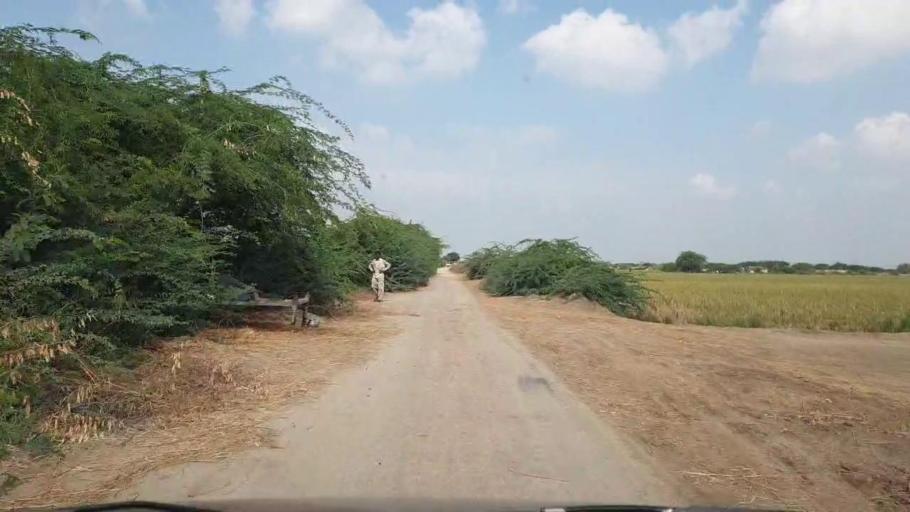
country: PK
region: Sindh
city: Badin
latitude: 24.4685
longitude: 68.5902
